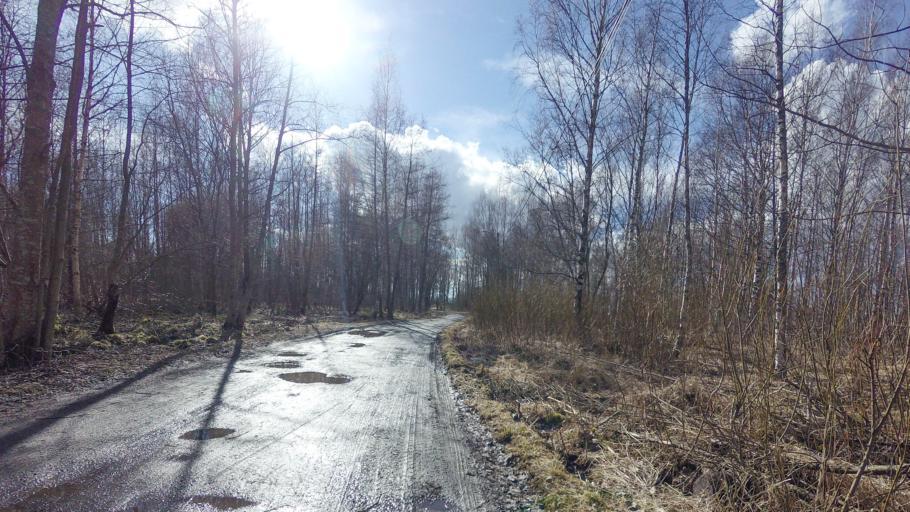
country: FI
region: Uusimaa
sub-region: Helsinki
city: Vantaa
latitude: 60.2048
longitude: 25.0224
